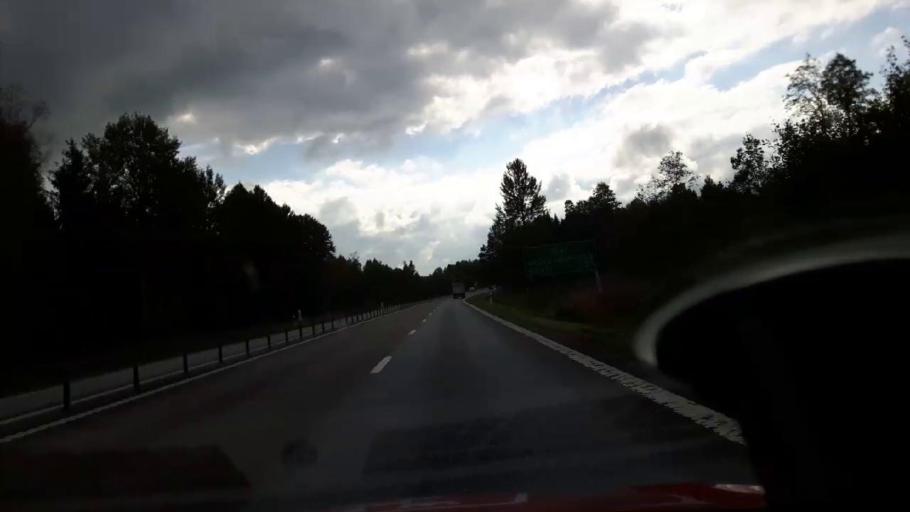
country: SE
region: Gaevleborg
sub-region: Gavle Kommun
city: Norrsundet
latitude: 60.9543
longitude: 17.0332
